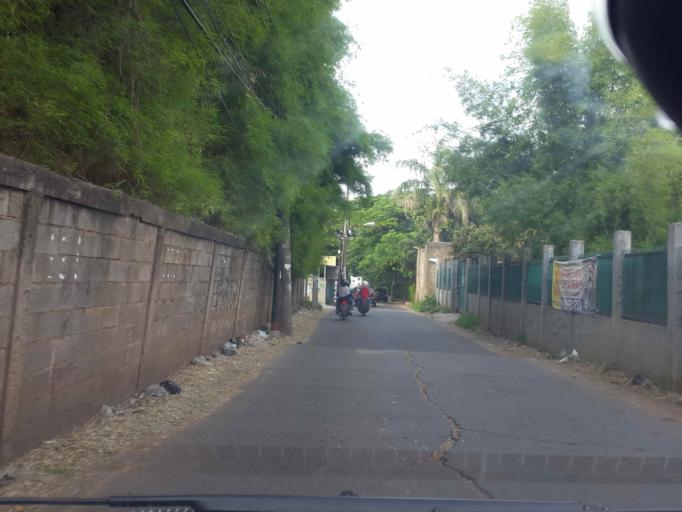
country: ID
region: West Java
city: Ciputat
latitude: -6.2574
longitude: 106.6692
